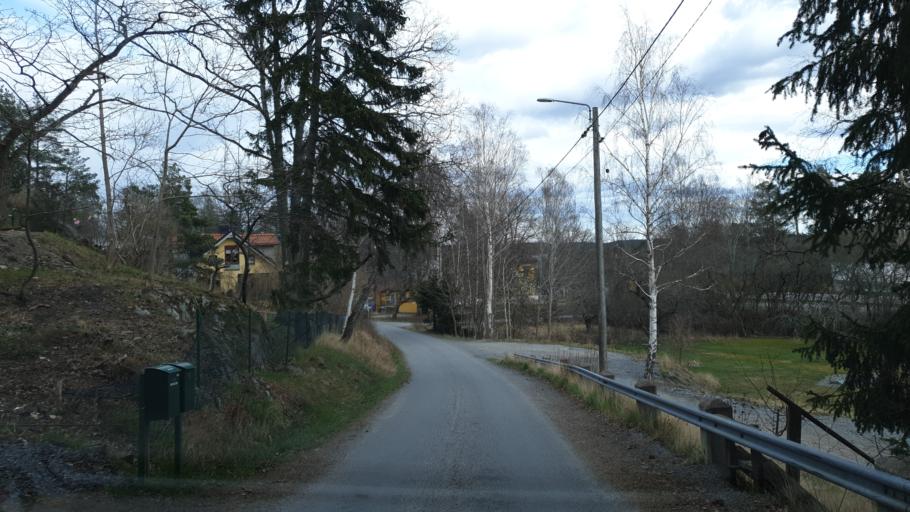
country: SE
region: Stockholm
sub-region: Nacka Kommun
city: Boo
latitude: 59.3216
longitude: 18.3064
